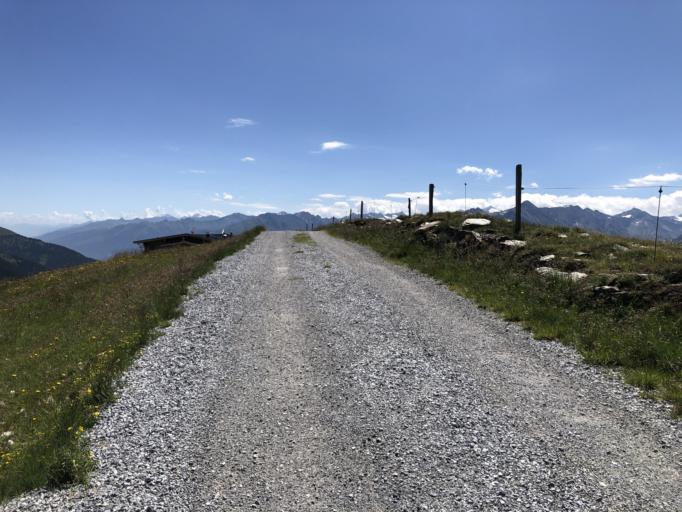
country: AT
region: Salzburg
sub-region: Politischer Bezirk Zell am See
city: Krimml
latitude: 47.2587
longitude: 12.0987
